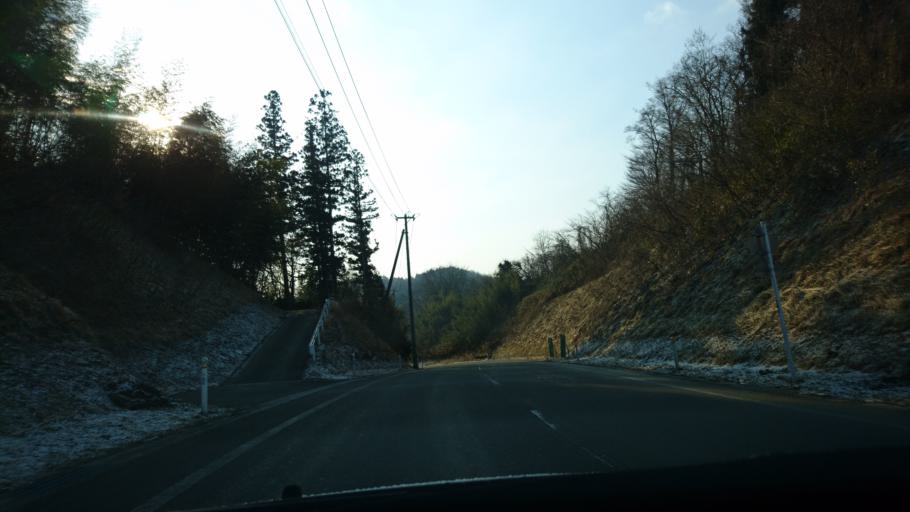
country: JP
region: Iwate
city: Ichinoseki
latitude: 38.9214
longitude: 141.3514
